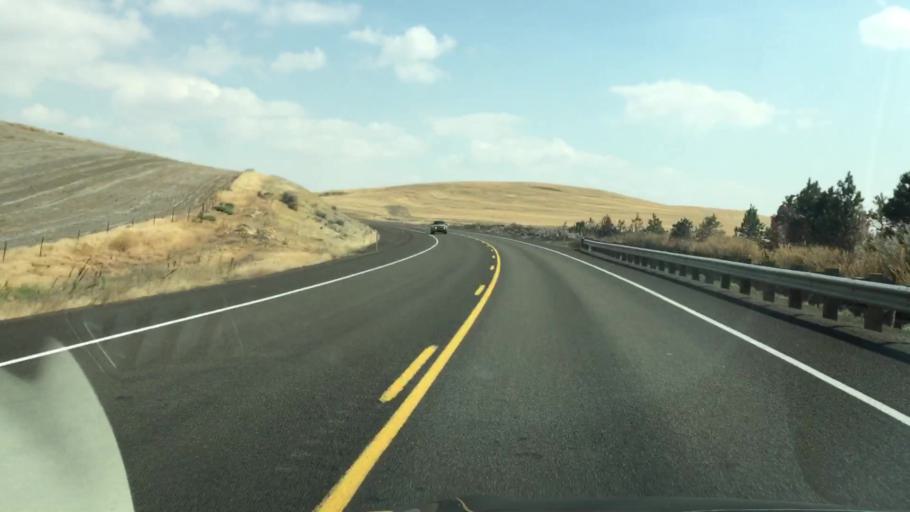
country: US
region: Oregon
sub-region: Wasco County
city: The Dalles
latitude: 45.4924
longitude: -121.0949
